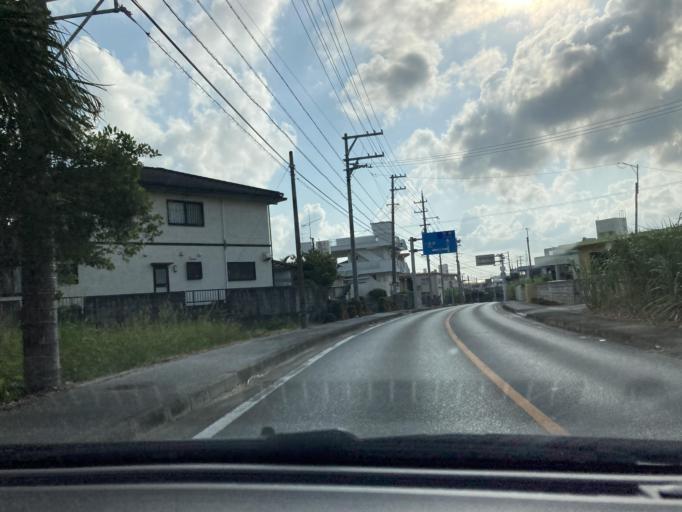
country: JP
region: Okinawa
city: Itoman
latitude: 26.1379
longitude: 127.6999
